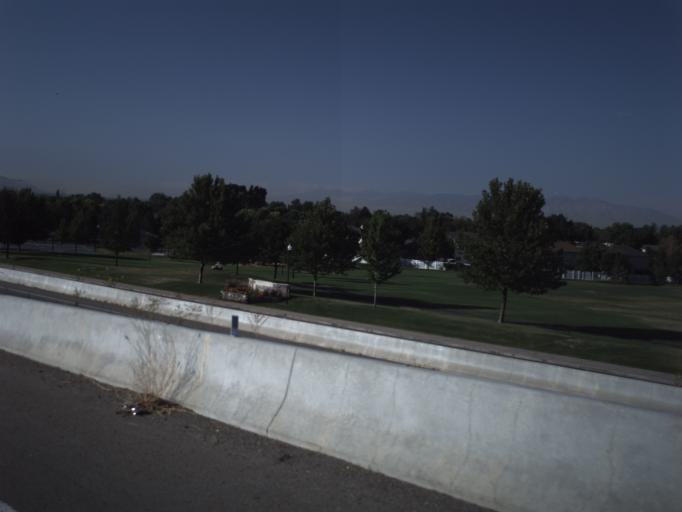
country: US
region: Utah
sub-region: Davis County
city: Fruit Heights
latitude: 41.0085
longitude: -111.9121
